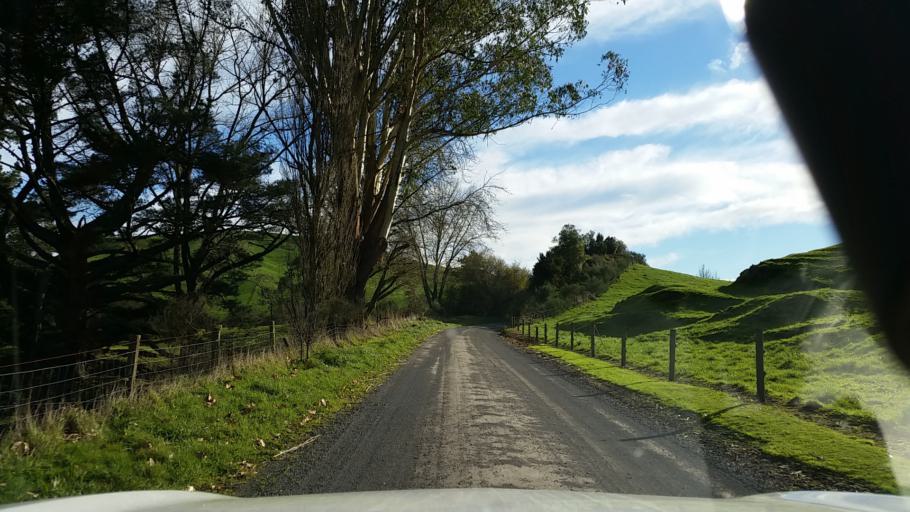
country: NZ
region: Waikato
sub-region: South Waikato District
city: Tokoroa
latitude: -38.3768
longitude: 176.0861
